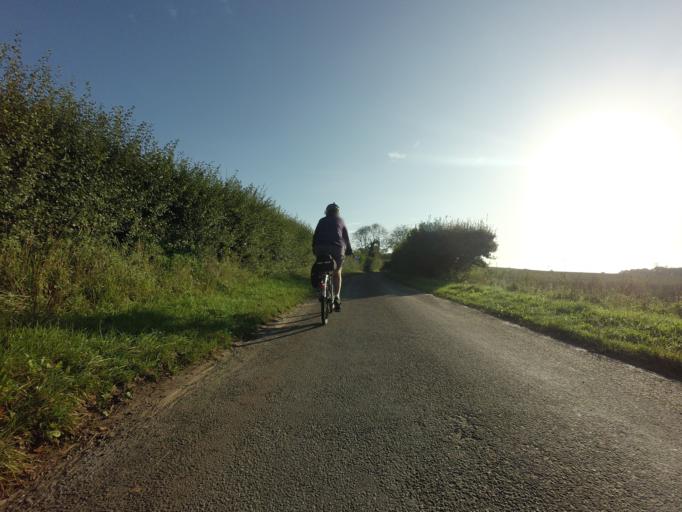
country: GB
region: England
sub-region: Norfolk
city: Dersingham
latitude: 52.8208
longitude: 0.5227
